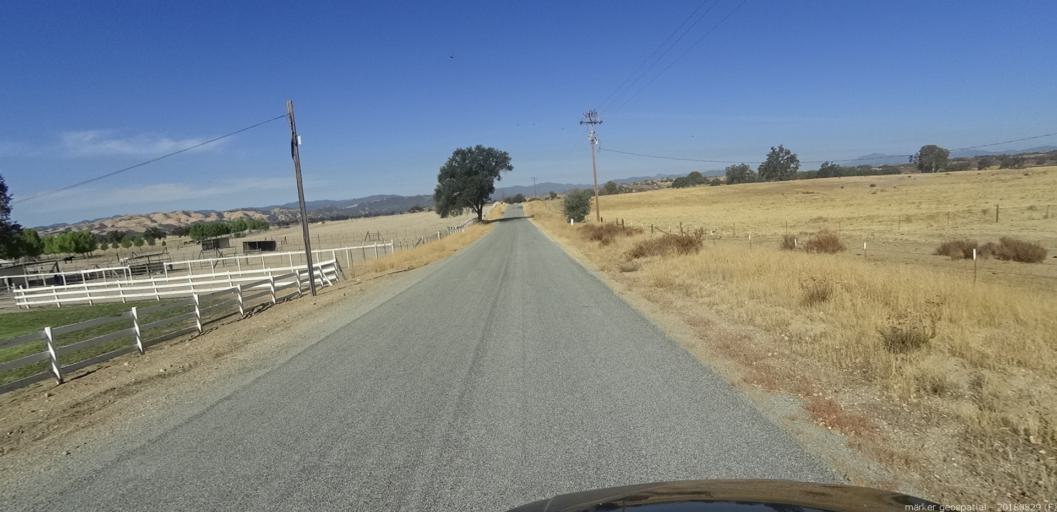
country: US
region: California
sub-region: Monterey County
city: King City
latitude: 35.9661
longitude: -121.1298
